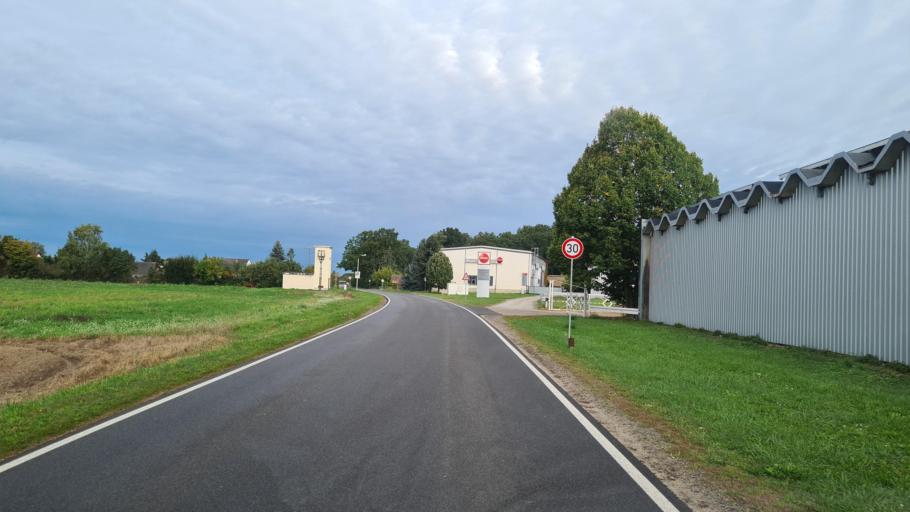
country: DE
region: Brandenburg
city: Luckau
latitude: 51.8661
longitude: 13.7316
